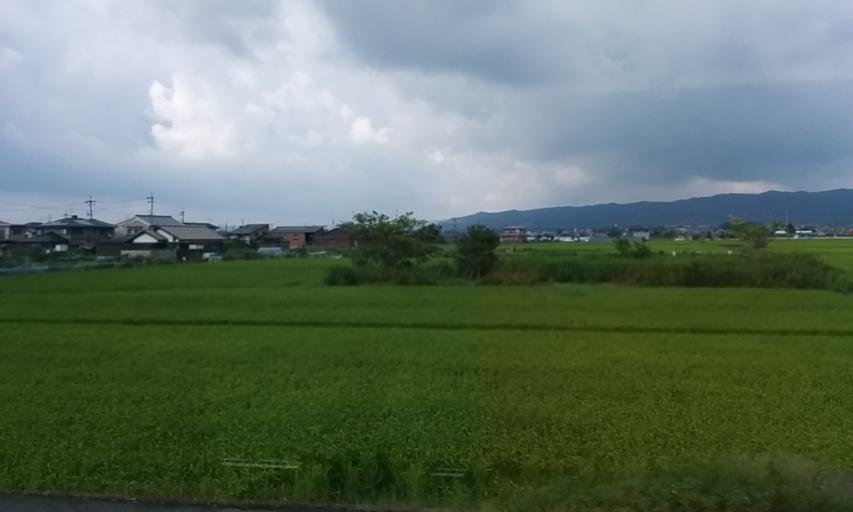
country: JP
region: Nara
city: Nara-shi
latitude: 34.6321
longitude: 135.7810
